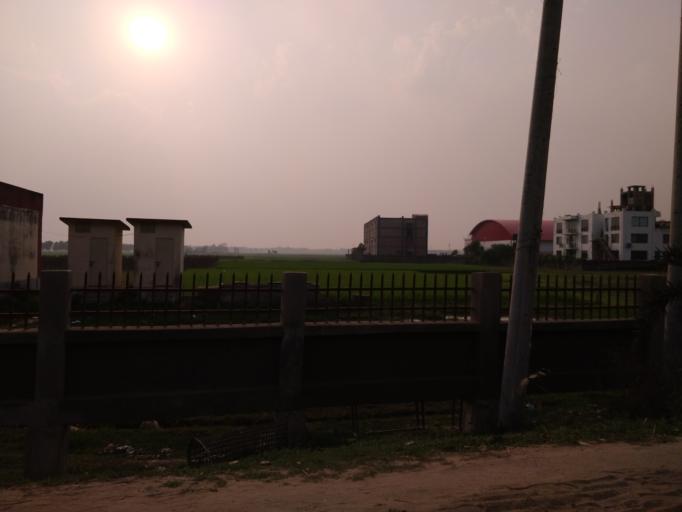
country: IN
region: Tripura
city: Khowai
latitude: 24.1331
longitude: 91.3520
